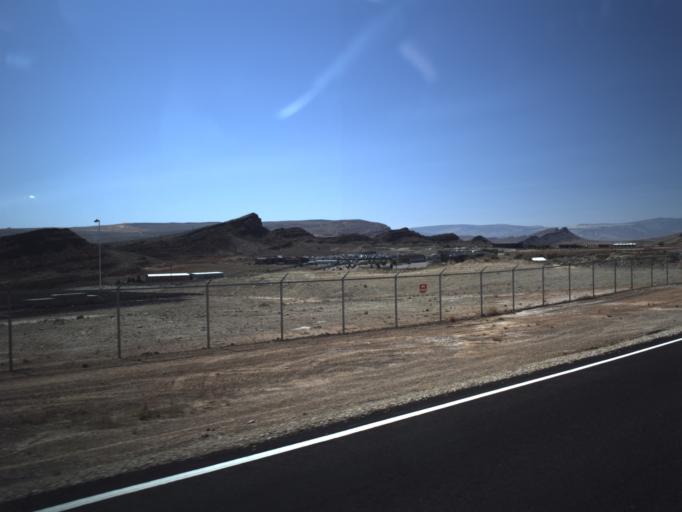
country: US
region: Utah
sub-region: Washington County
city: Hurricane
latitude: 37.1727
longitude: -113.4029
